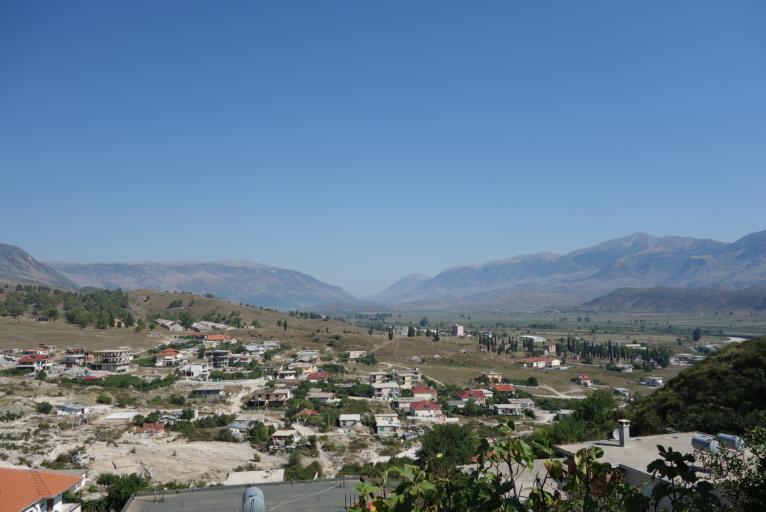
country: AL
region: Gjirokaster
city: Gjirokaster
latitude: 40.0837
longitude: 20.1356
